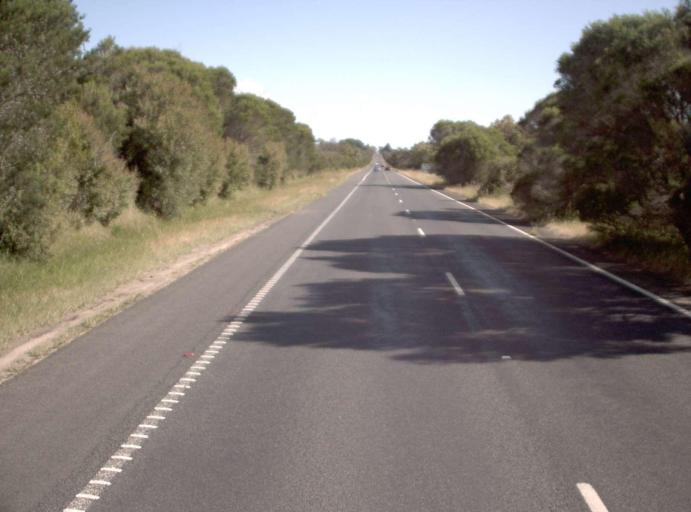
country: AU
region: Victoria
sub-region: Cardinia
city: Koo-Wee-Rup
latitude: -38.2923
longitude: 145.5455
